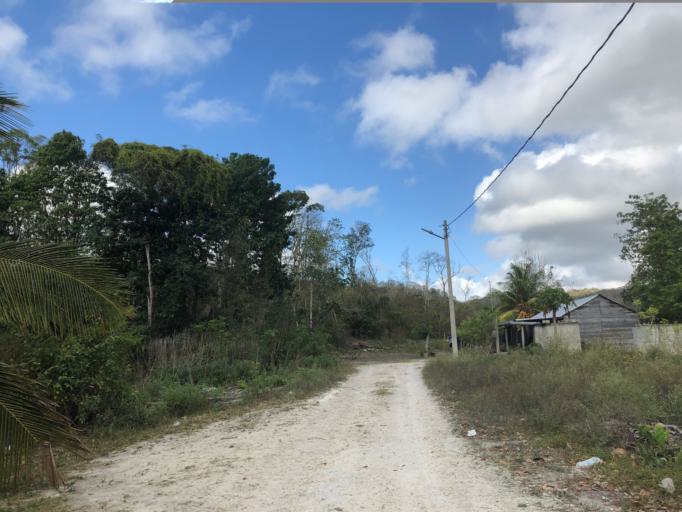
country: MX
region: Quintana Roo
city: Nicolas Bravo
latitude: 18.4562
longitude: -89.3063
